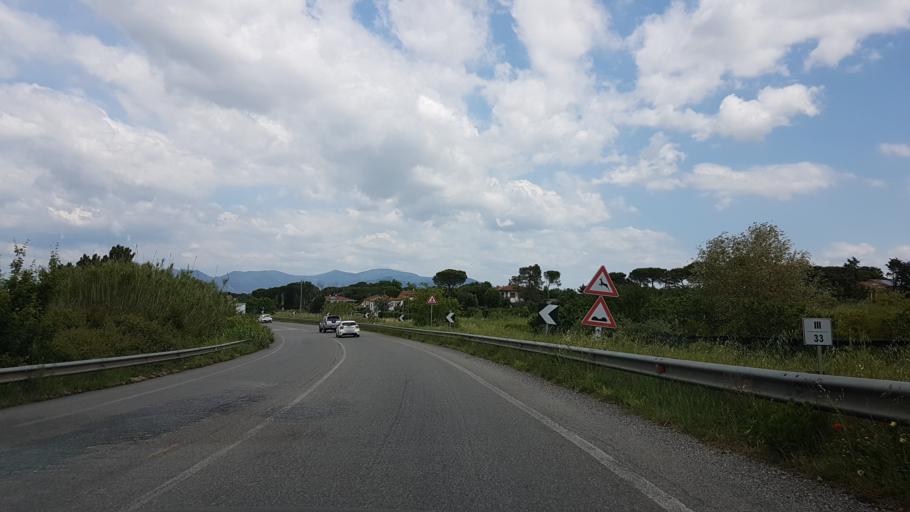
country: IT
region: Tuscany
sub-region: Provincia di Livorno
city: Collesalvetti
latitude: 43.6007
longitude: 10.4750
